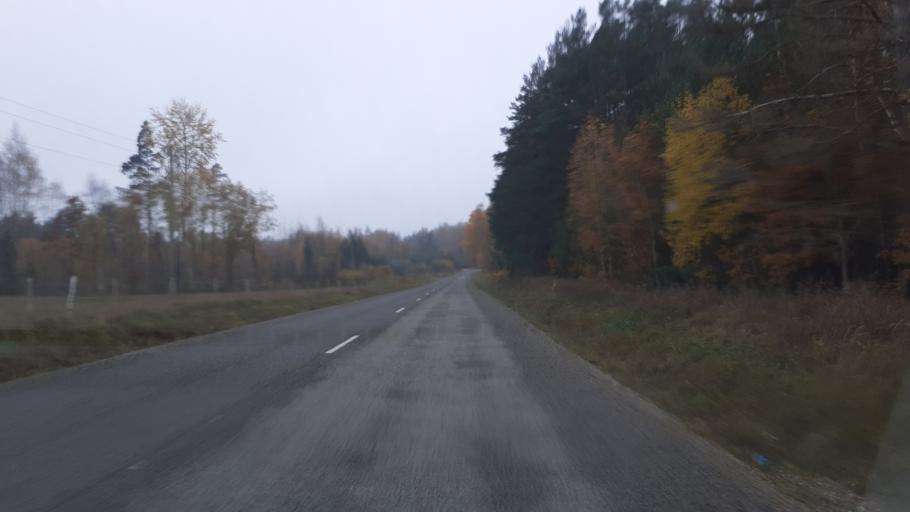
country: LV
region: Kuldigas Rajons
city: Kuldiga
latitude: 56.9575
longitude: 21.8870
